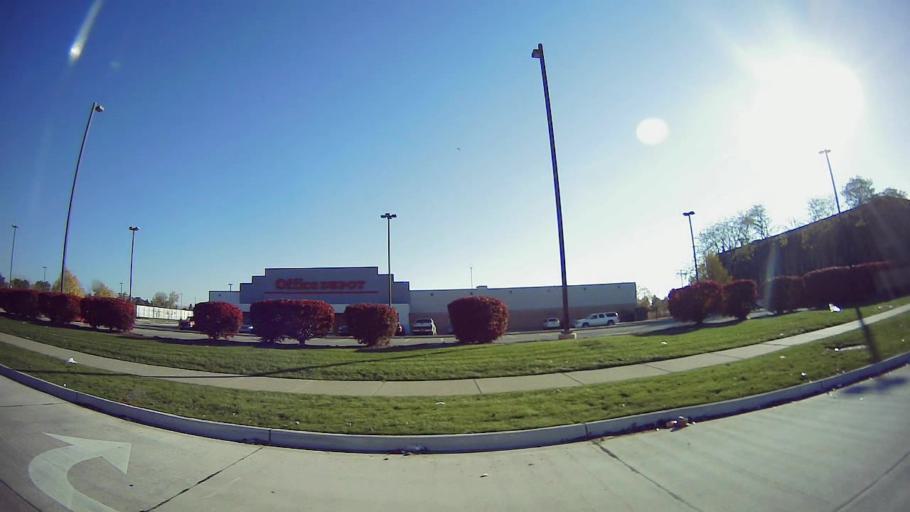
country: US
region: Michigan
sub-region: Oakland County
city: Oak Park
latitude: 42.4485
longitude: -83.2005
